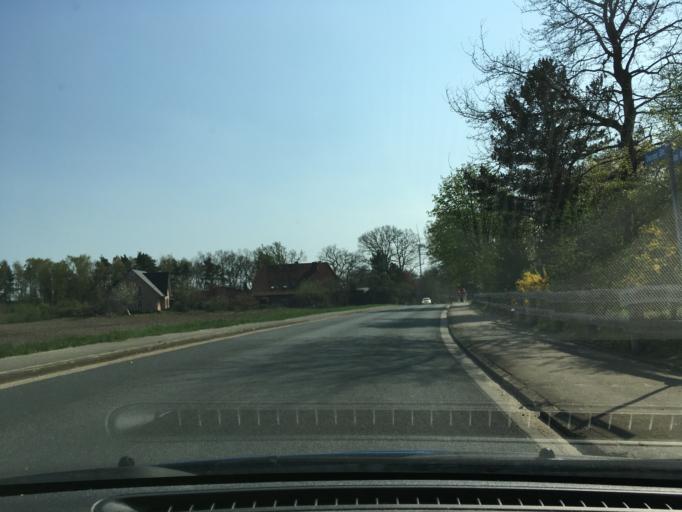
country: DE
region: Lower Saxony
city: Sudergellersen
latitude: 53.2072
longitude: 10.3002
